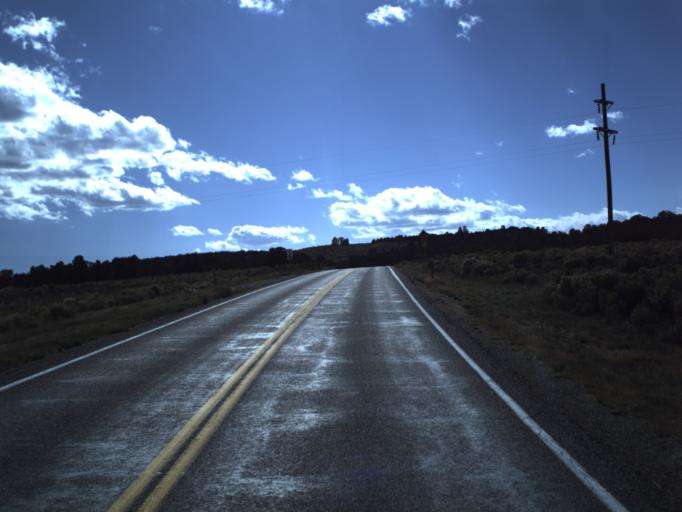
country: US
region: Utah
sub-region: Garfield County
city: Panguitch
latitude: 37.7723
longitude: -112.4455
